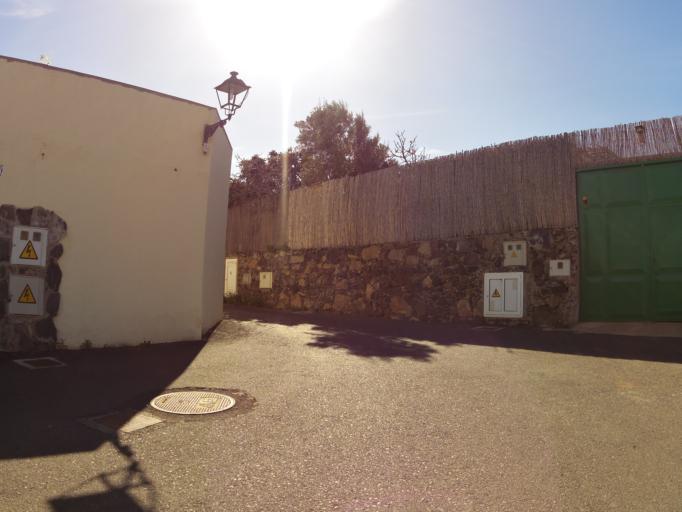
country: ES
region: Canary Islands
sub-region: Provincia de Las Palmas
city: Aguimes
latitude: 27.9072
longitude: -15.4496
